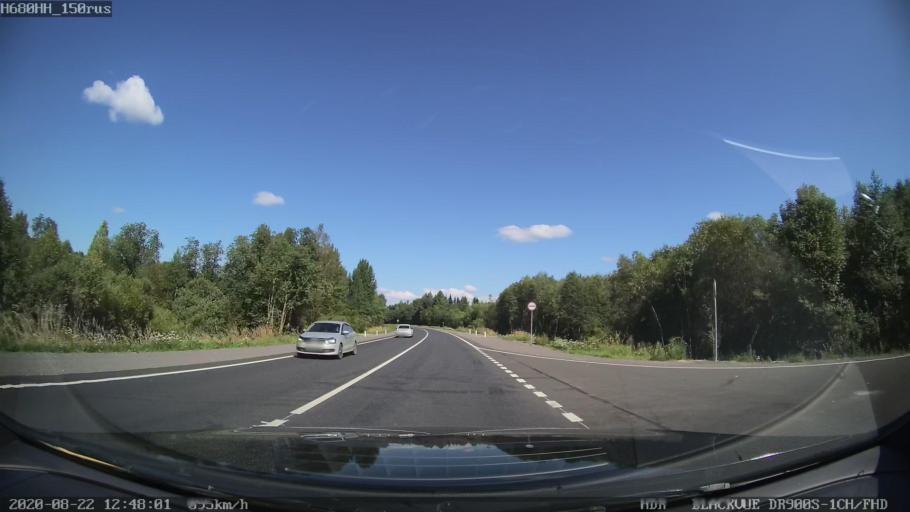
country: RU
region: Tverskaya
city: Rameshki
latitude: 57.4341
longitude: 36.1796
